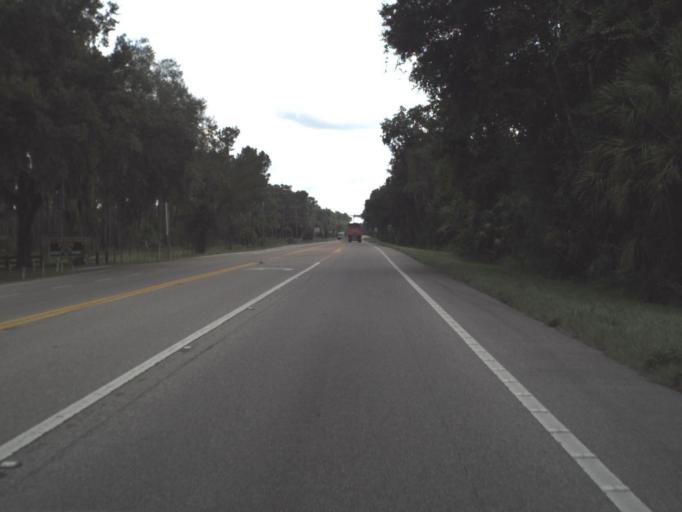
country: US
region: Florida
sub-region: Pasco County
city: Crystal Springs
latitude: 28.1399
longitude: -82.2274
